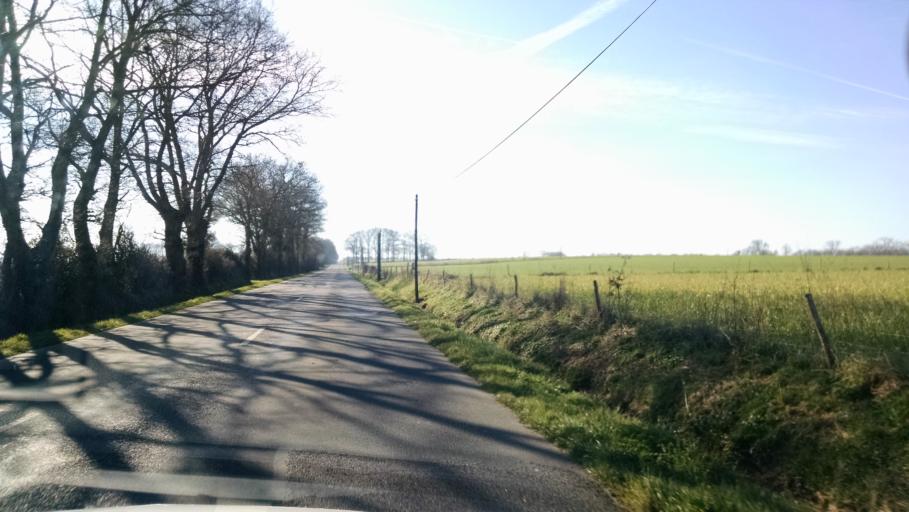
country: FR
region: Pays de la Loire
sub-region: Departement de la Loire-Atlantique
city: Vieillevigne
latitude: 46.9587
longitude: -1.4218
